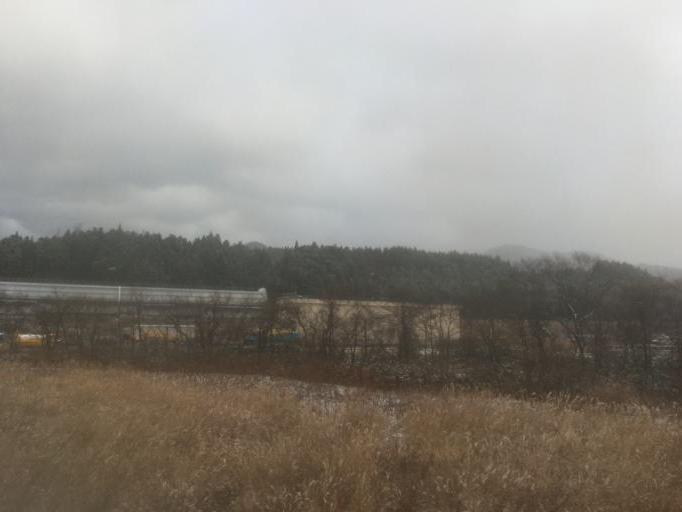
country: JP
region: Aomori
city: Goshogawara
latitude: 41.1400
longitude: 140.5175
